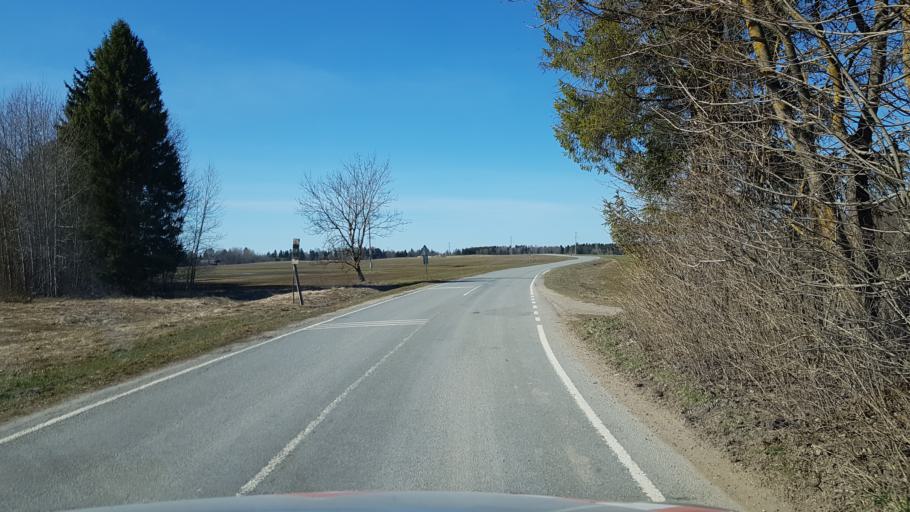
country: EE
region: Laeaene-Virumaa
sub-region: Someru vald
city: Someru
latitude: 59.3502
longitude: 26.4857
